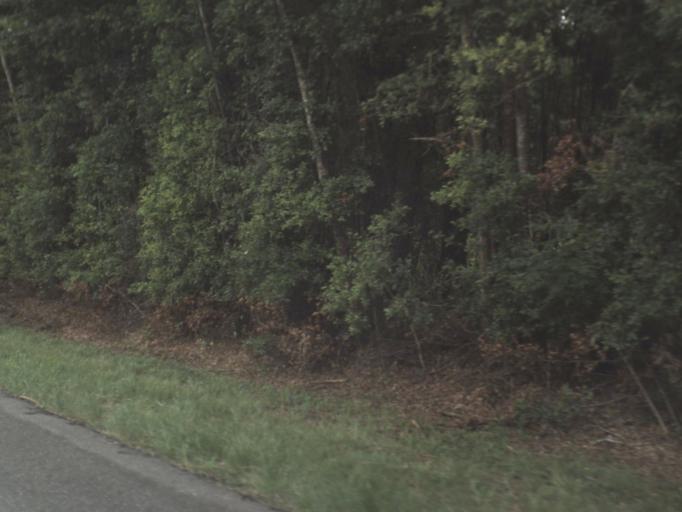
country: US
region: Florida
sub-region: Alachua County
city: Newberry
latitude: 29.5957
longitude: -82.5683
